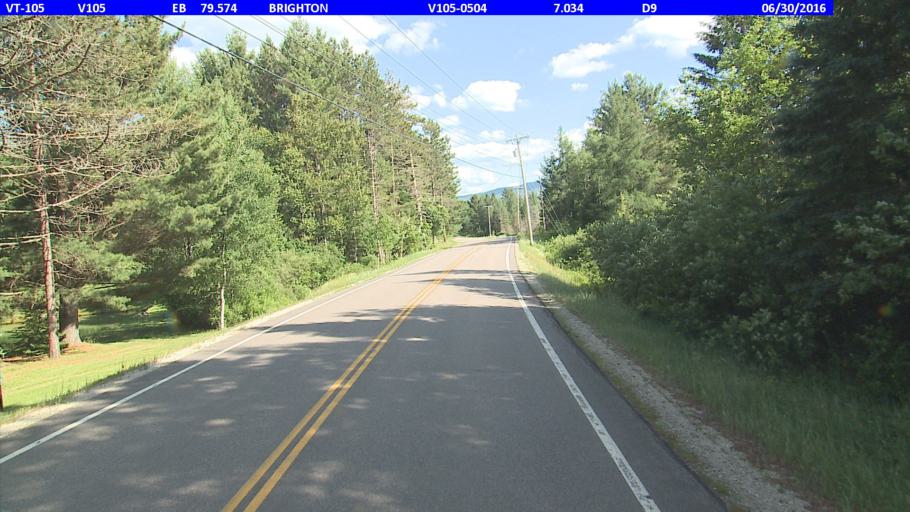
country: US
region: Vermont
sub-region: Caledonia County
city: Lyndonville
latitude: 44.7984
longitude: -71.8399
